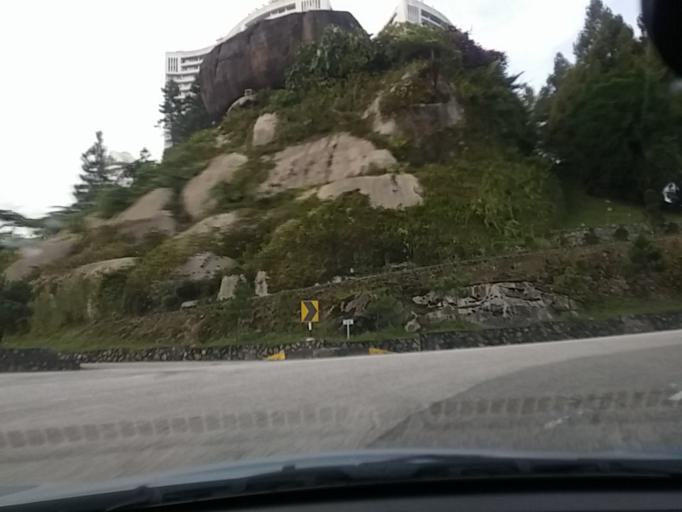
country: MY
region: Pahang
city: Kampung Bukit Tinggi, Bentong
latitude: 3.4181
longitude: 101.7896
